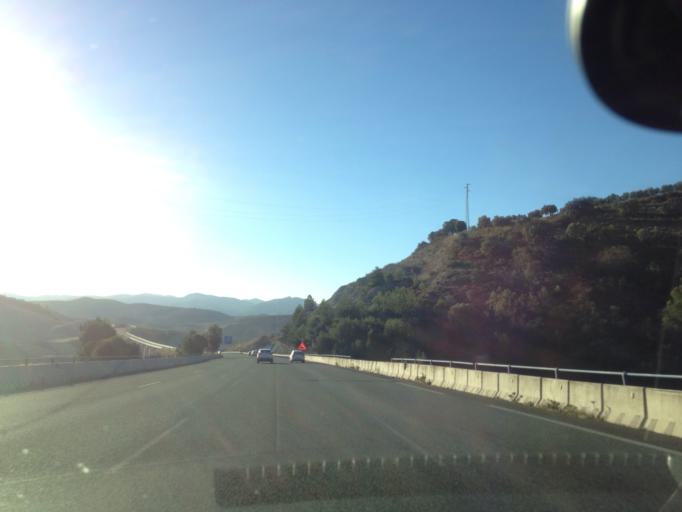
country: ES
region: Andalusia
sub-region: Provincia de Malaga
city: Casabermeja
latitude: 36.9538
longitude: -4.4464
